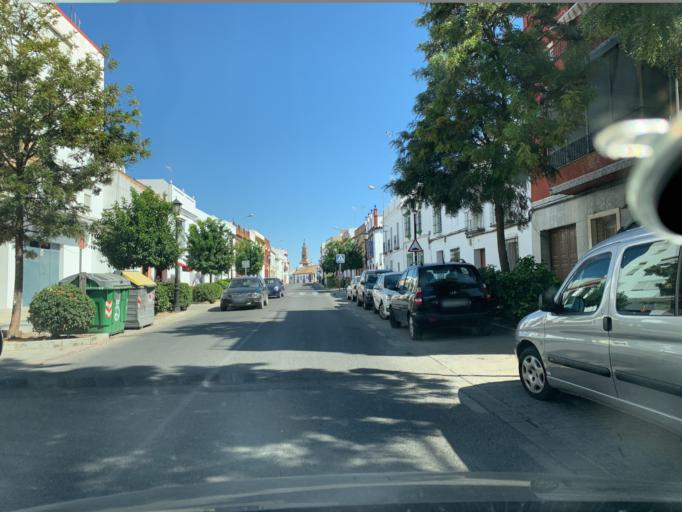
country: ES
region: Andalusia
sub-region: Provincia de Sevilla
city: Carmona
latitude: 37.4686
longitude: -5.6472
